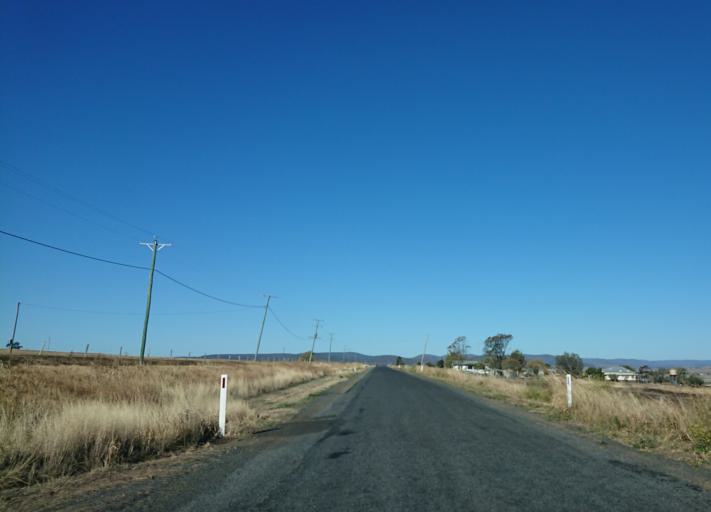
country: AU
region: Queensland
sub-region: Toowoomba
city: Top Camp
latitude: -27.8104
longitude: 151.9640
